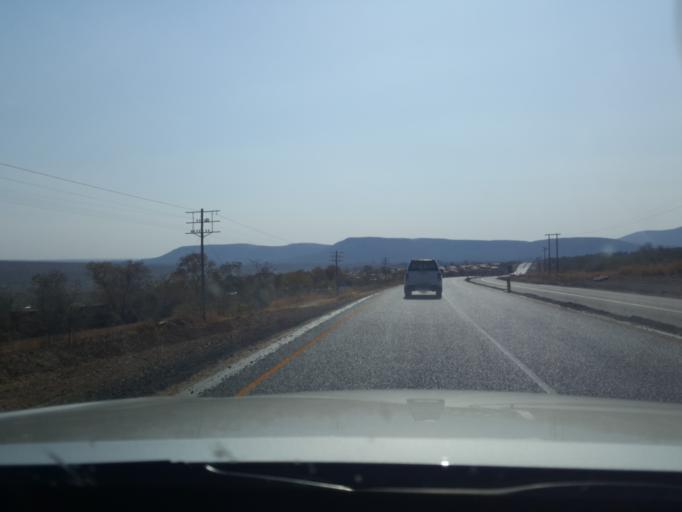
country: ZA
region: North-West
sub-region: Ngaka Modiri Molema District Municipality
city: Zeerust
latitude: -25.6054
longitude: 26.4379
